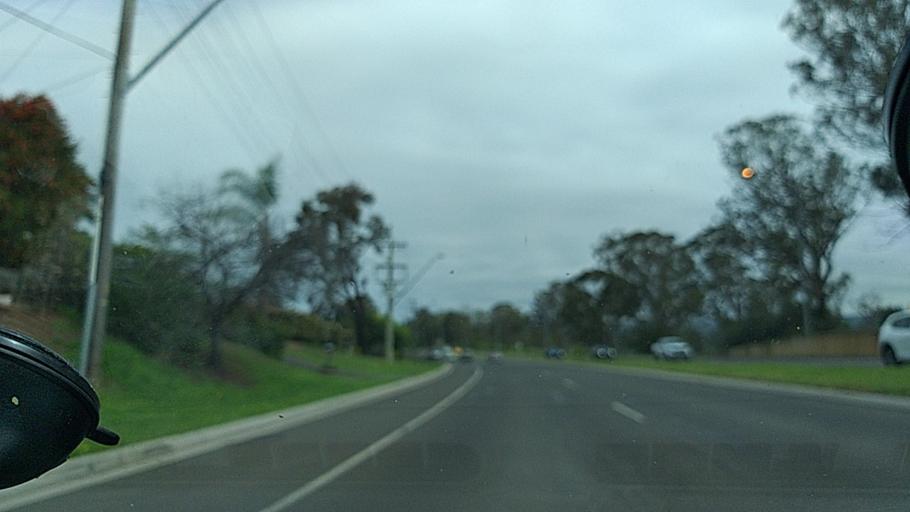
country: AU
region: New South Wales
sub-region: Camden
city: Camden South
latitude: -34.0947
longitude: 150.6947
